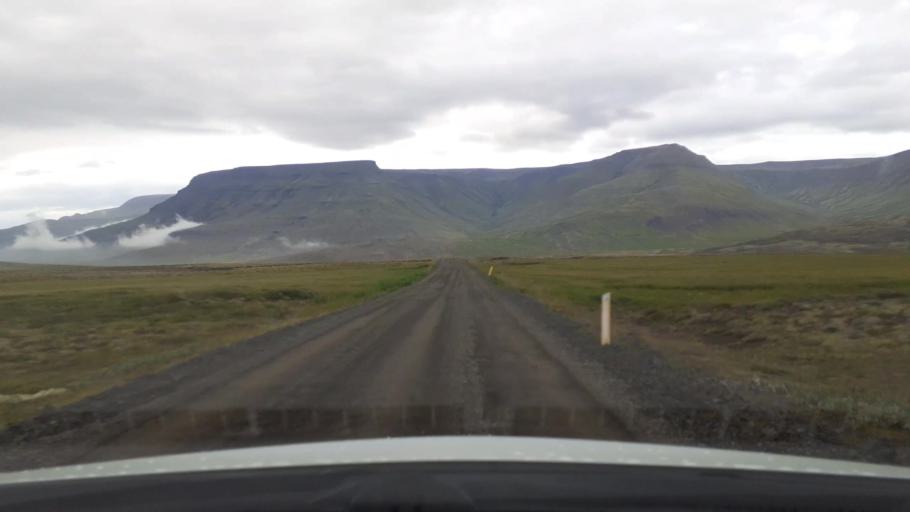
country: IS
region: Capital Region
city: Mosfellsbaer
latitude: 64.1943
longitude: -21.5447
